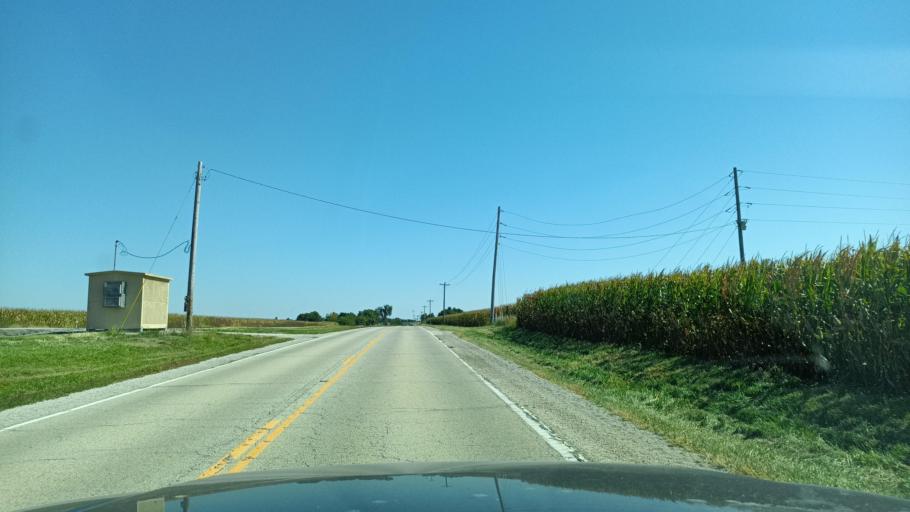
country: US
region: Illinois
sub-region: Woodford County
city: Eureka
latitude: 40.6269
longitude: -89.3096
